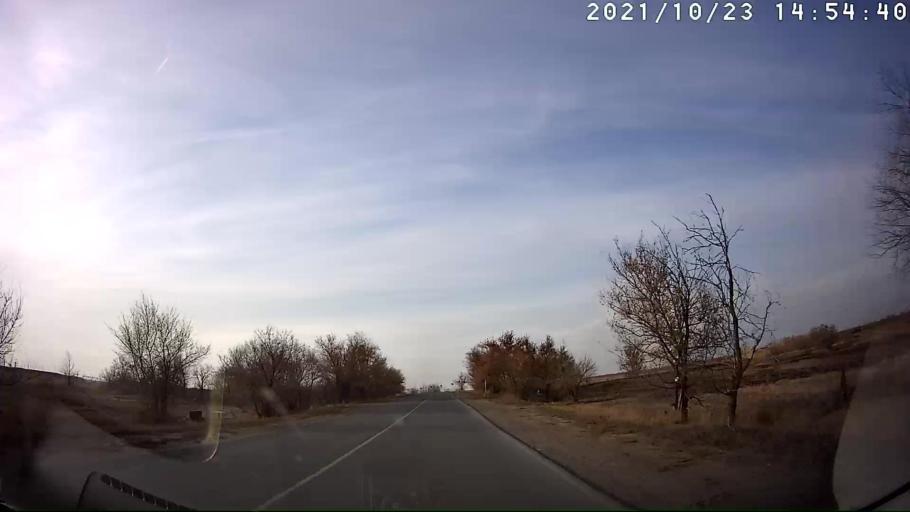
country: RU
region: Volgograd
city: Volgograd
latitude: 48.4502
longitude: 44.4122
